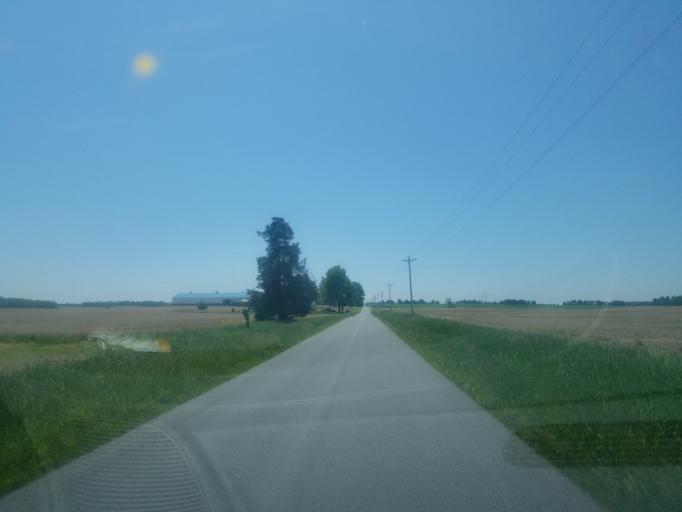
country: US
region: Ohio
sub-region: Huron County
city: New London
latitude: 41.1069
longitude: -82.4627
